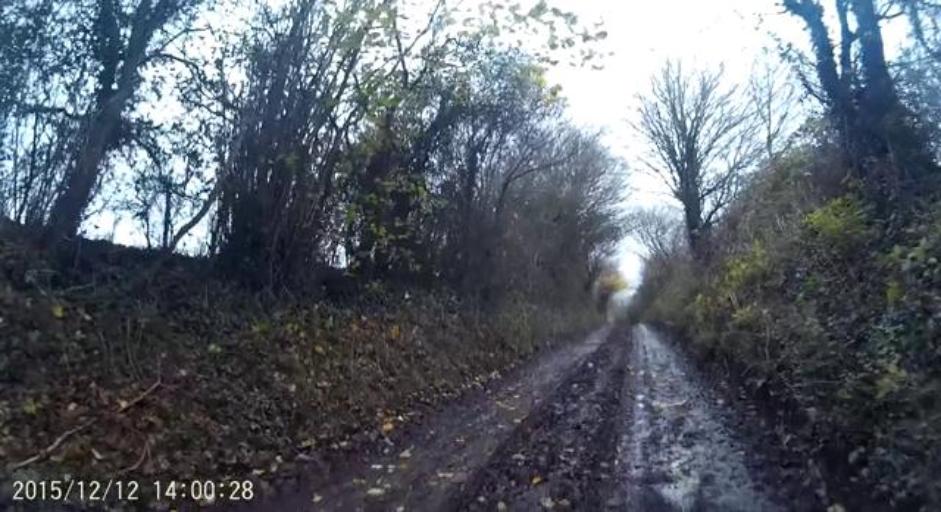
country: GB
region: England
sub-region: West Sussex
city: Milland
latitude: 50.9648
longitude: -0.8393
